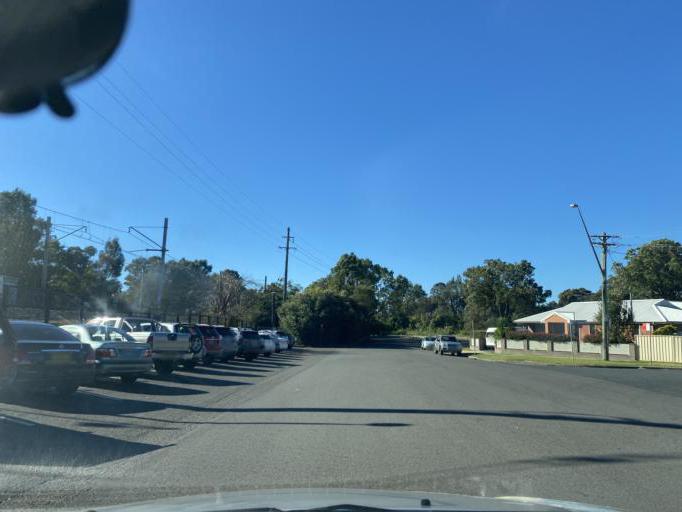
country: AU
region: New South Wales
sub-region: Campbelltown Municipality
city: Ingleburn
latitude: -33.9845
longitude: 150.8795
